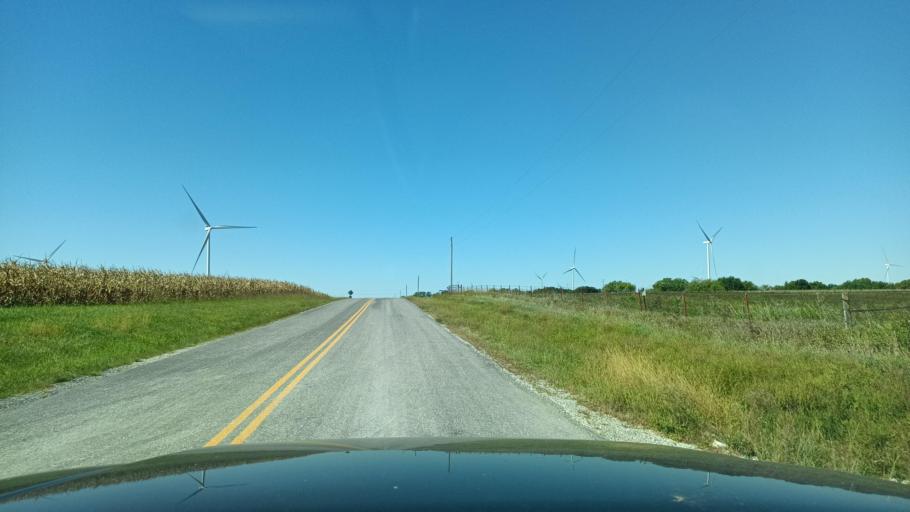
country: US
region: Missouri
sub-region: Adair County
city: Kirksville
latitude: 40.3306
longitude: -92.4790
